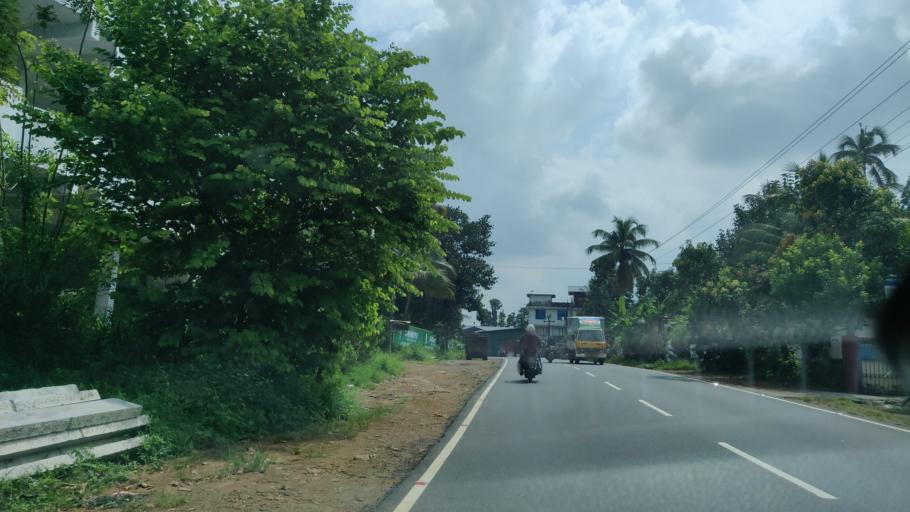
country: IN
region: Kerala
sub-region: Ernakulam
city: Angamali
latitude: 10.1691
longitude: 76.4233
